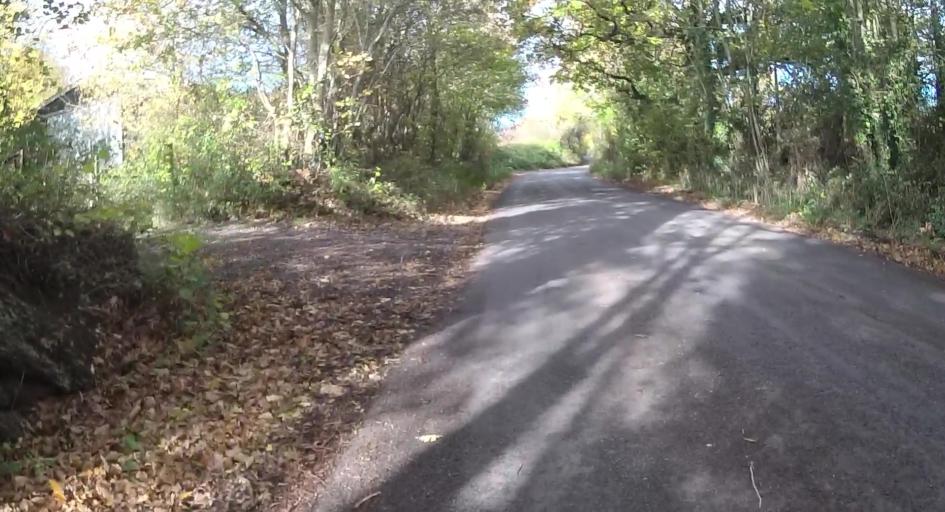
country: GB
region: England
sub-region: Hampshire
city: Basingstoke
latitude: 51.3216
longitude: -1.0720
